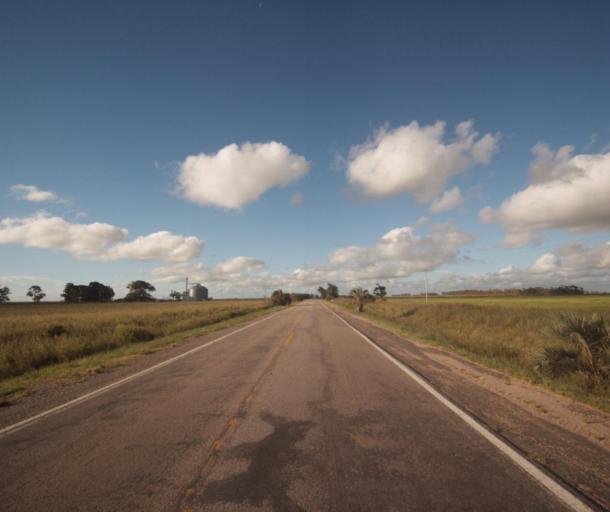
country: BR
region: Rio Grande do Sul
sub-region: Arroio Grande
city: Arroio Grande
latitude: -32.4475
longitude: -52.5697
